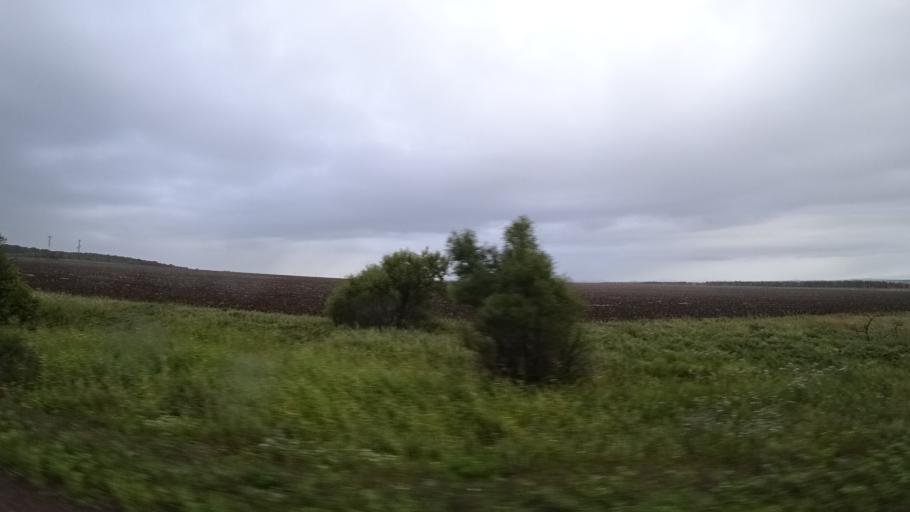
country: RU
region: Primorskiy
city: Chernigovka
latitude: 44.3646
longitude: 132.5423
